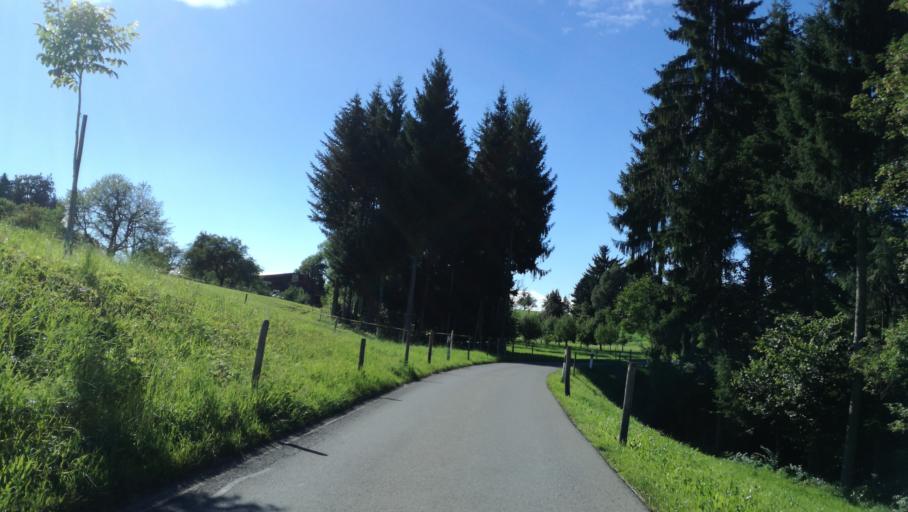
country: CH
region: Zug
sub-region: Zug
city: Zug
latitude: 47.1601
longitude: 8.5489
